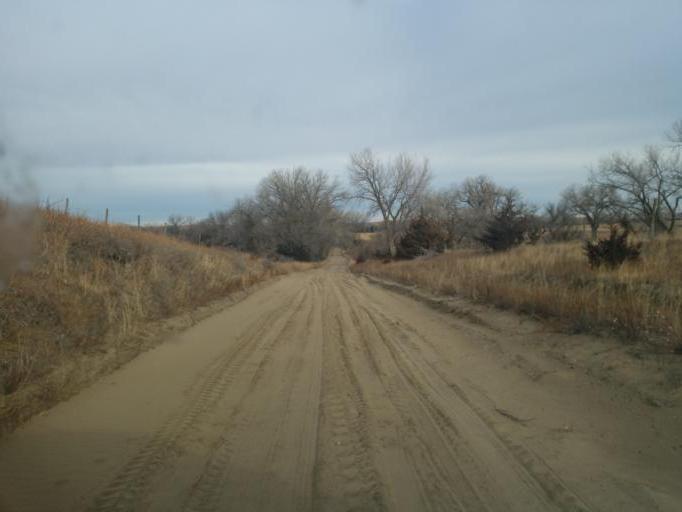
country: US
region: Nebraska
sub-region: Knox County
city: Center
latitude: 42.6087
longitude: -97.8379
